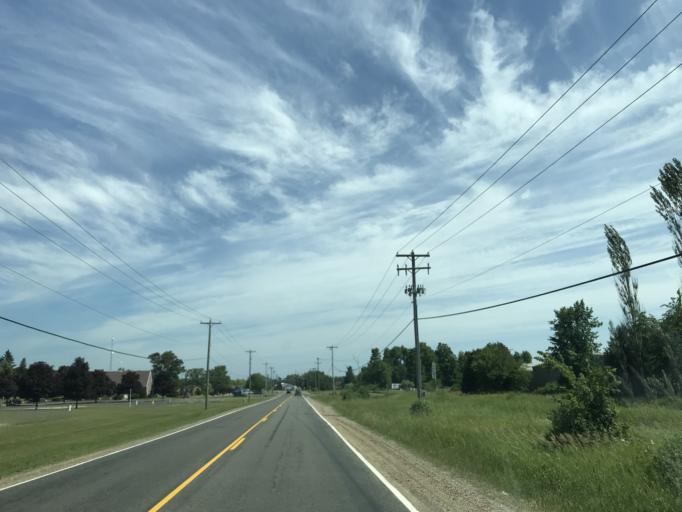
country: US
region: Michigan
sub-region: Grand Traverse County
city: Traverse City
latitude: 44.7129
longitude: -85.6266
